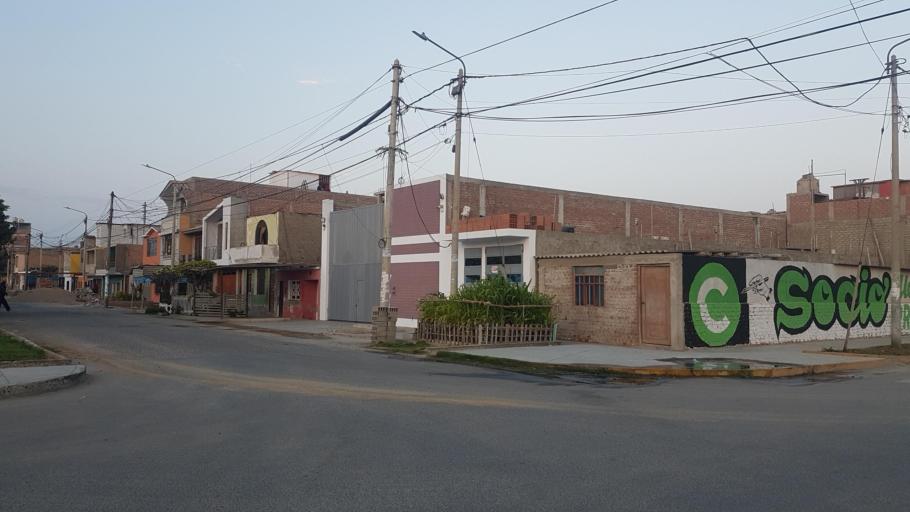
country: PE
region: Ancash
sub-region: Provincia de Santa
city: Chimbote
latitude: -9.0925
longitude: -78.5735
